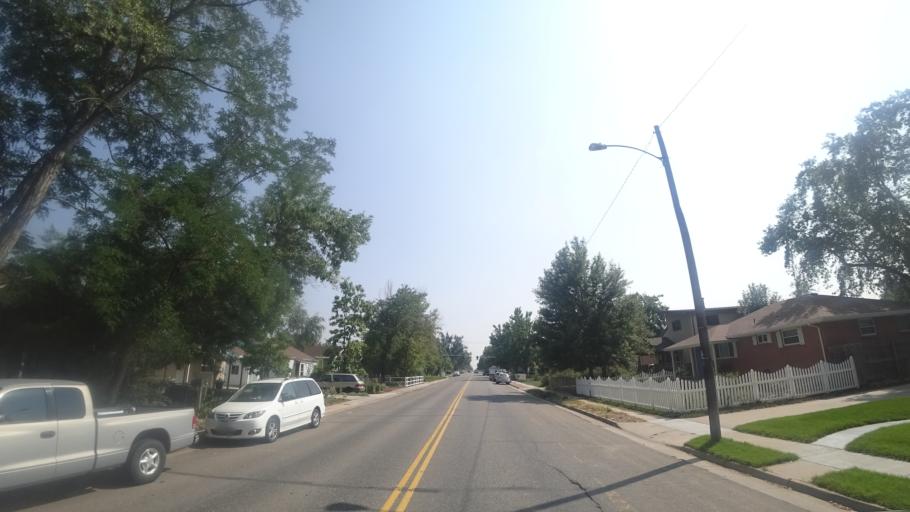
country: US
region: Colorado
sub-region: Arapahoe County
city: Englewood
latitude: 39.6433
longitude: -104.9831
